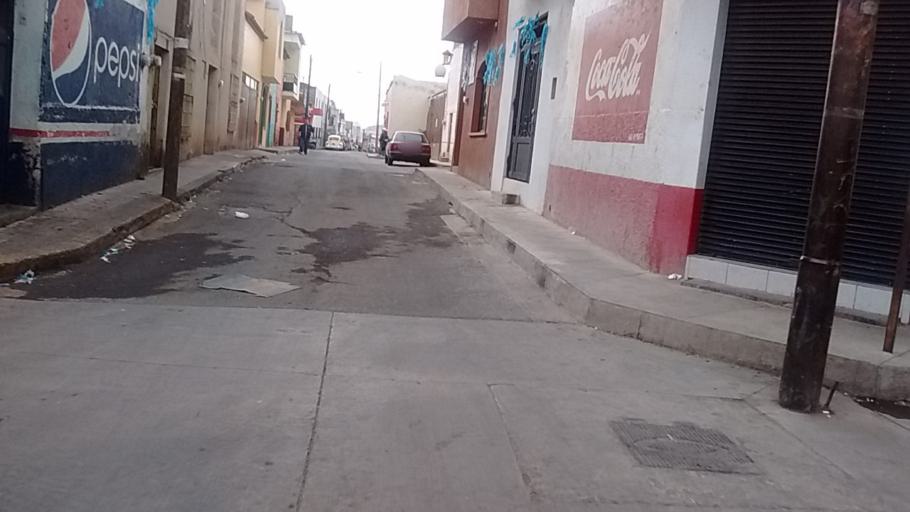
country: MX
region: Jalisco
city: Atotonilco el Alto
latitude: 20.5472
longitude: -102.5076
